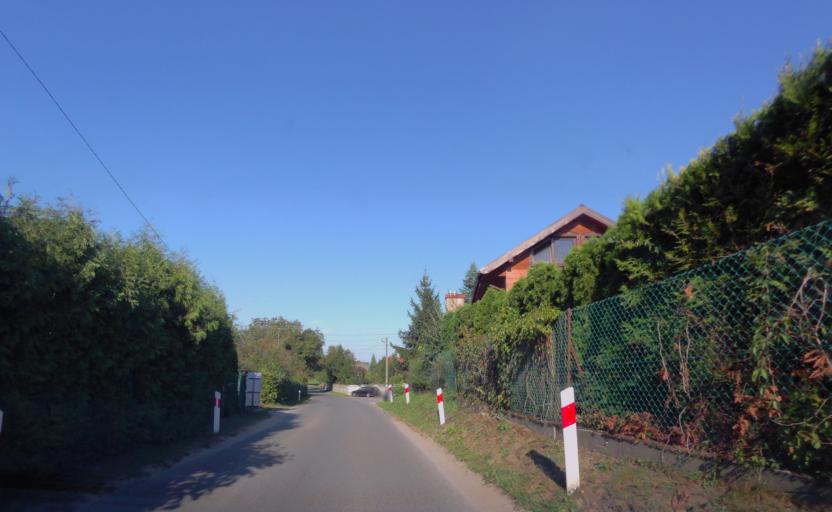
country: PL
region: Subcarpathian Voivodeship
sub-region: Powiat lezajski
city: Stare Miasto
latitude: 50.2928
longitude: 22.4025
